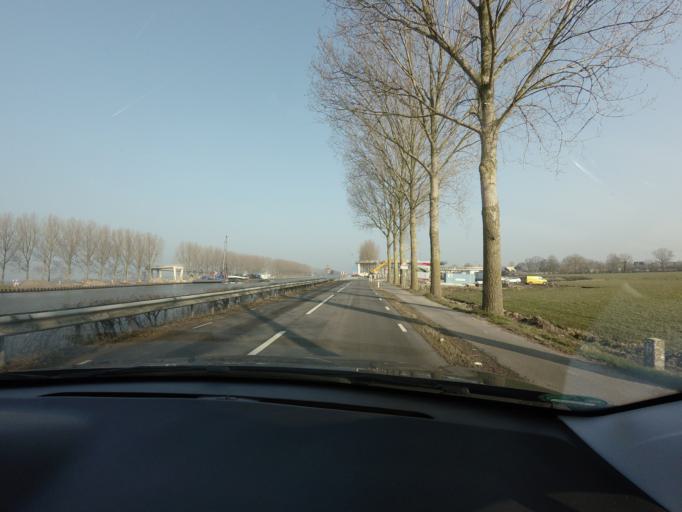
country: NL
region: North Holland
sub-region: Gemeente Amsterdam
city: Driemond
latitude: 52.2672
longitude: 5.0187
